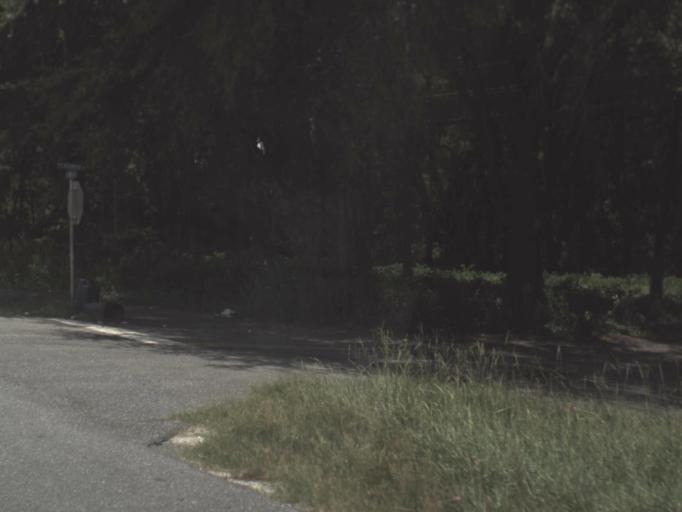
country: US
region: Florida
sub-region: Columbia County
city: Five Points
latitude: 30.3010
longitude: -82.7091
